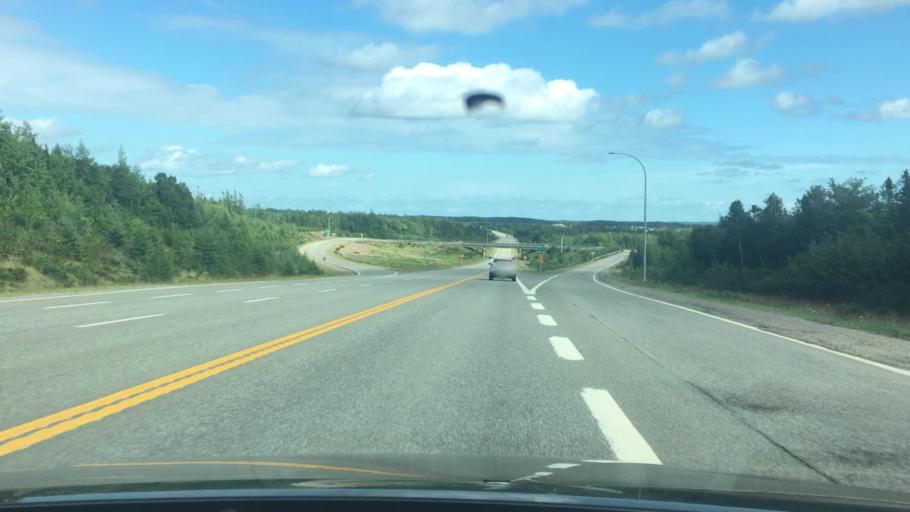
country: CA
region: Nova Scotia
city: Princeville
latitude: 45.6137
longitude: -61.0869
